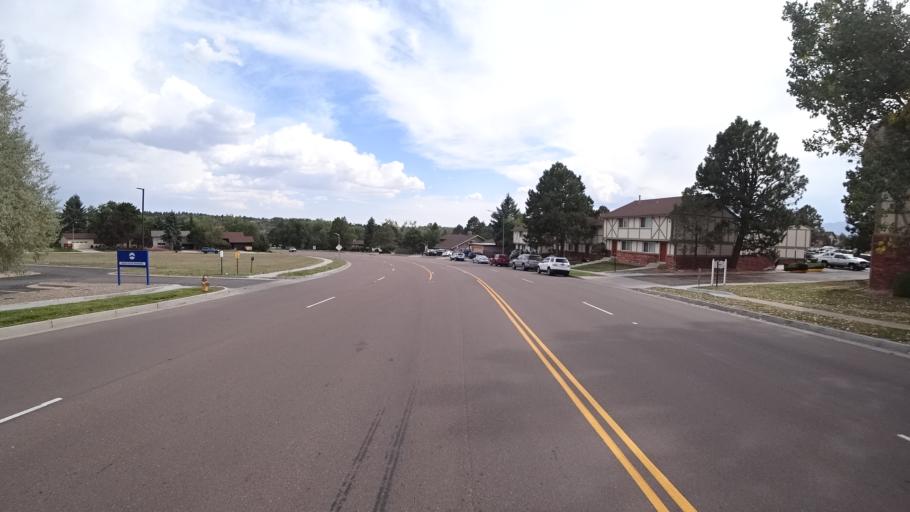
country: US
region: Colorado
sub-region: El Paso County
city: Cimarron Hills
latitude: 38.8768
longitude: -104.7544
